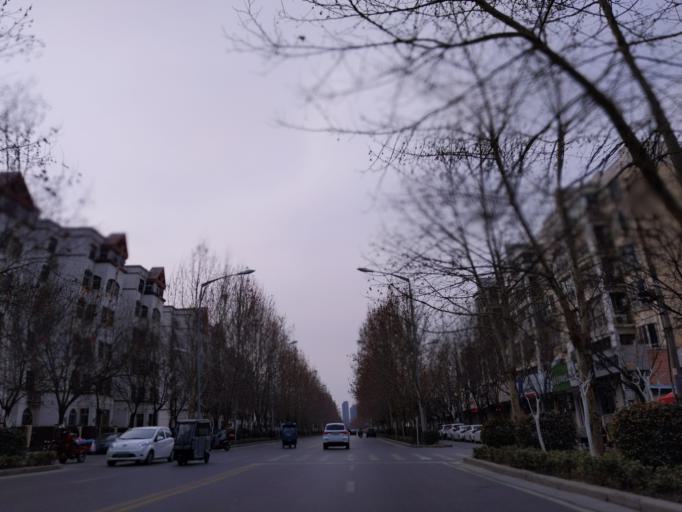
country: CN
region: Henan Sheng
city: Zhongyuanlu
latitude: 35.7574
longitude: 115.0523
